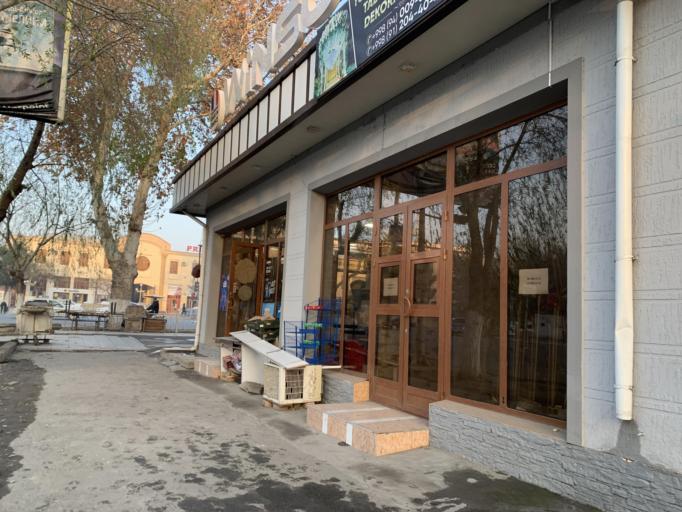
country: UZ
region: Fergana
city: Qo`qon
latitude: 40.5464
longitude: 70.9275
